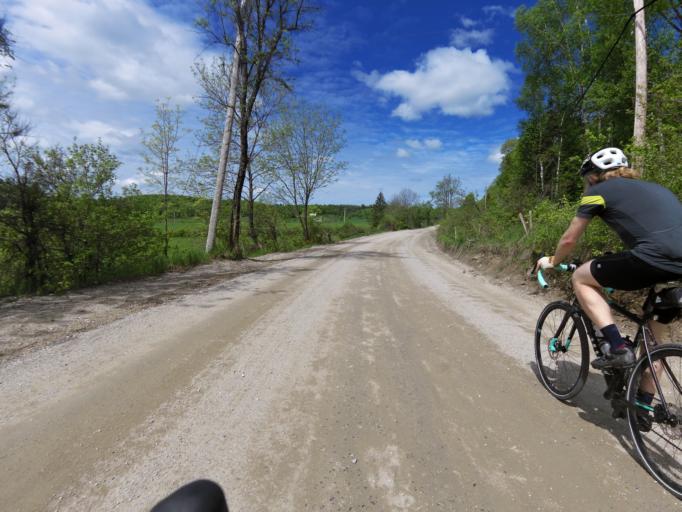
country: CA
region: Quebec
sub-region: Outaouais
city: Wakefield
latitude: 45.7838
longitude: -76.0043
